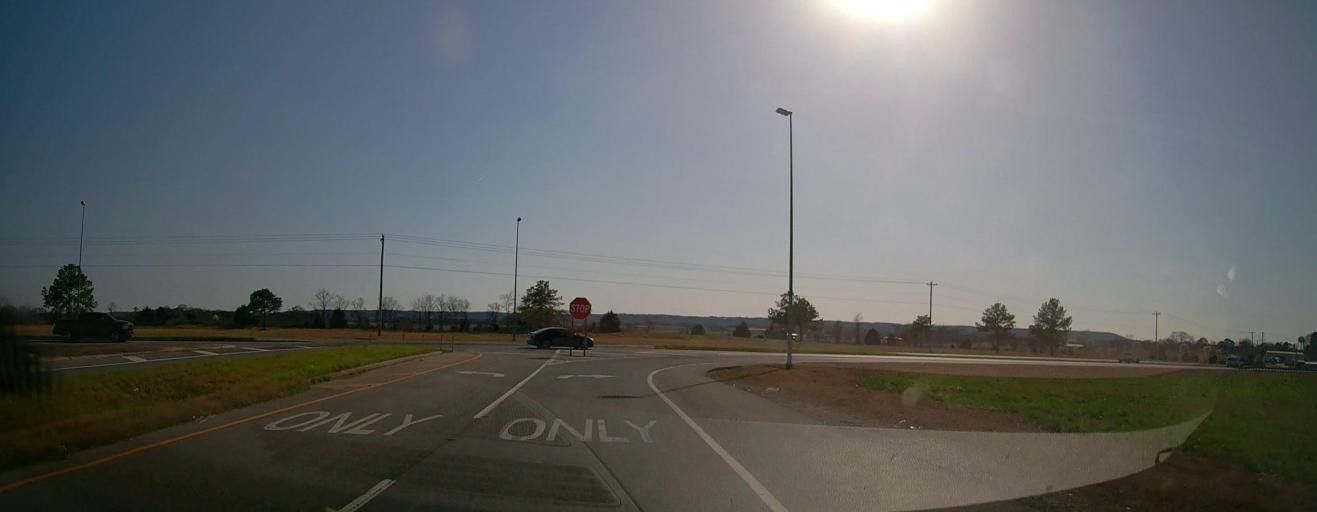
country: US
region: Alabama
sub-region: Colbert County
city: Muscle Shoals
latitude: 34.7006
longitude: -87.6401
